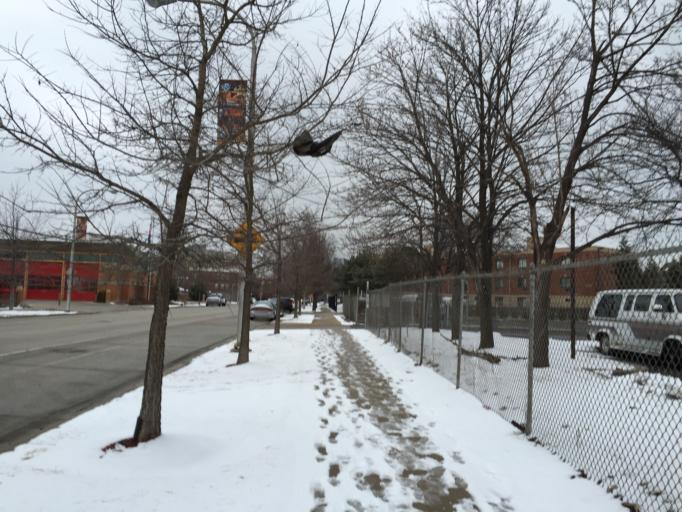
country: US
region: Illinois
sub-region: Cook County
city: Chicago
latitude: 41.8636
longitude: -87.6561
